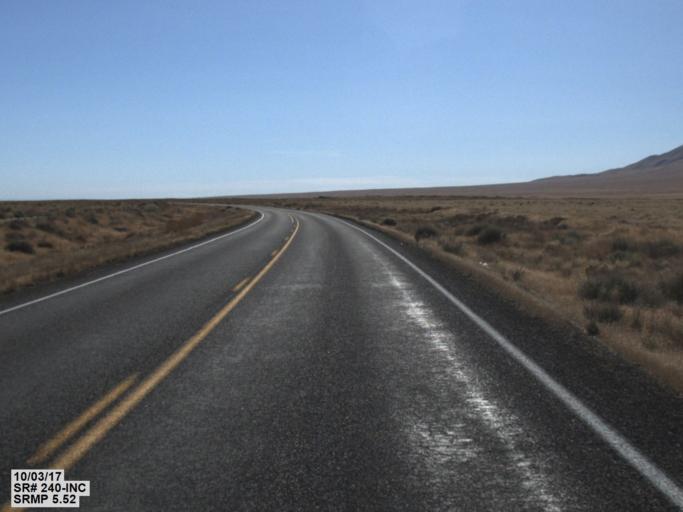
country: US
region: Washington
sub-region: Grant County
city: Desert Aire
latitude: 46.5137
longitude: -119.6640
